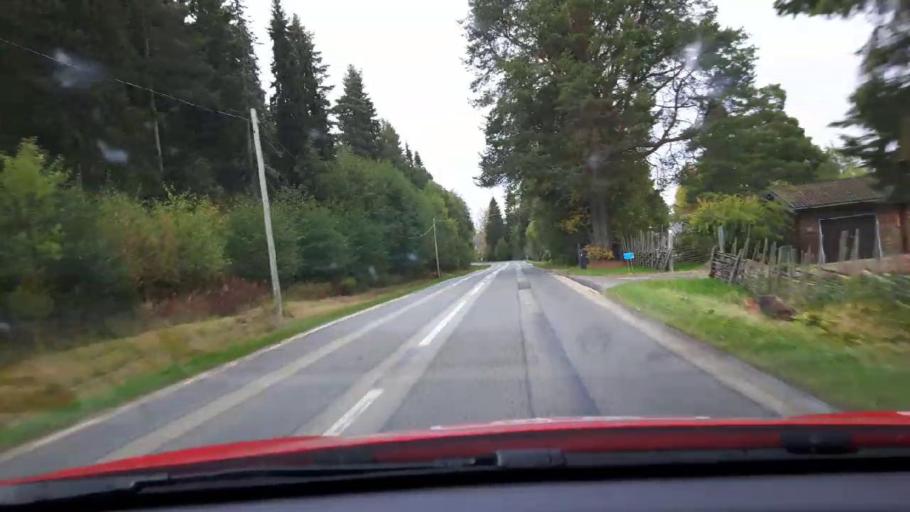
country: SE
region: Jaemtland
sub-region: Bergs Kommun
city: Hoverberg
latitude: 62.7858
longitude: 14.4364
